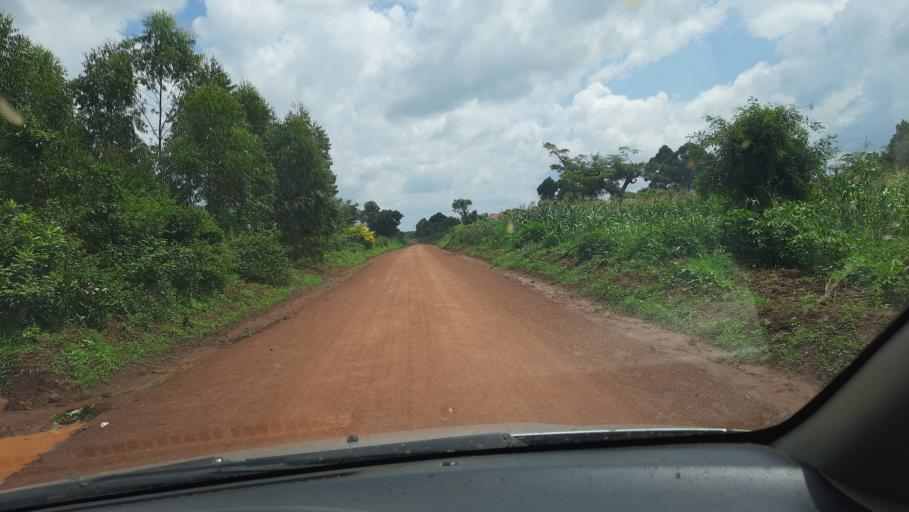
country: UG
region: Western Region
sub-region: Kiryandongo District
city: Kiryandongo
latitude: 1.8189
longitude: 31.9862
